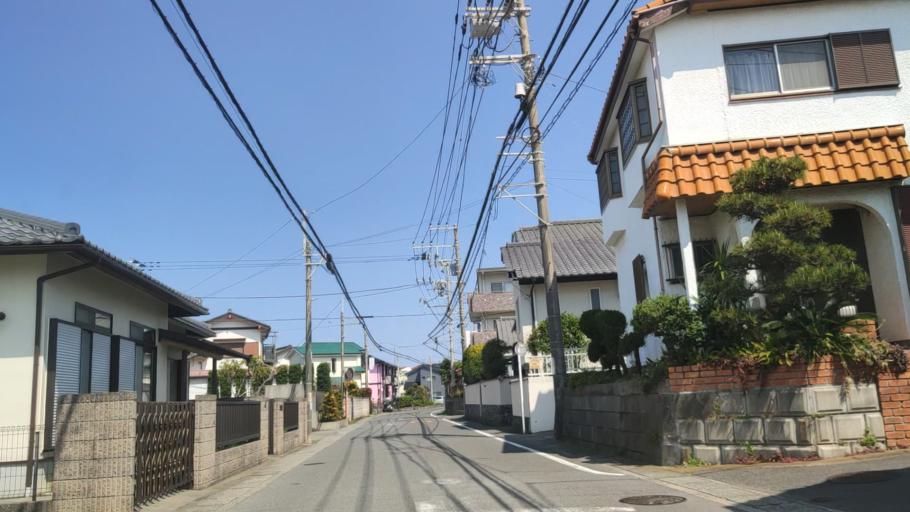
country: JP
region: Kanagawa
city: Hiratsuka
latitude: 35.3154
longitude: 139.3251
